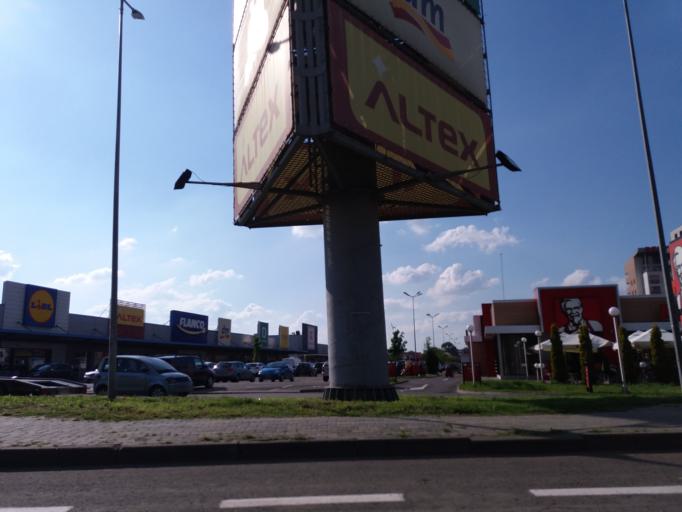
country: RO
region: Arad
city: Arad
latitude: 46.1849
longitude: 21.3155
